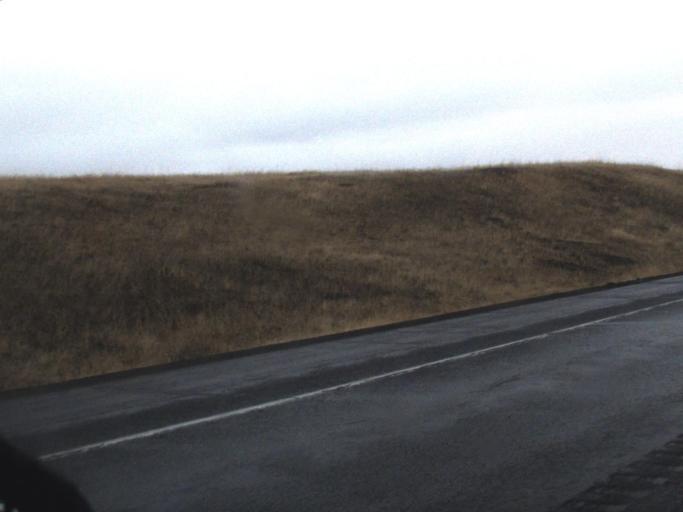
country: US
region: Washington
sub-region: Spokane County
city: Cheney
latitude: 47.2429
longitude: -117.3629
